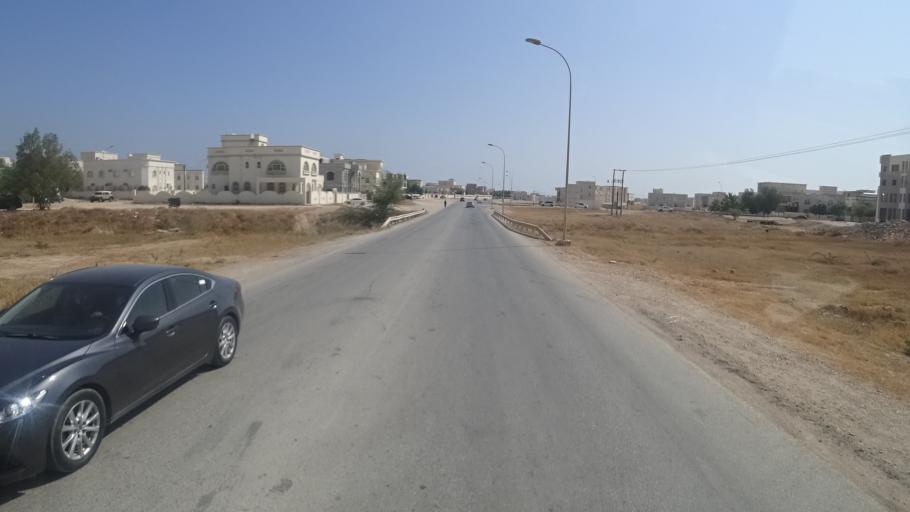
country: OM
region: Zufar
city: Salalah
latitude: 17.0116
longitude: 54.0247
